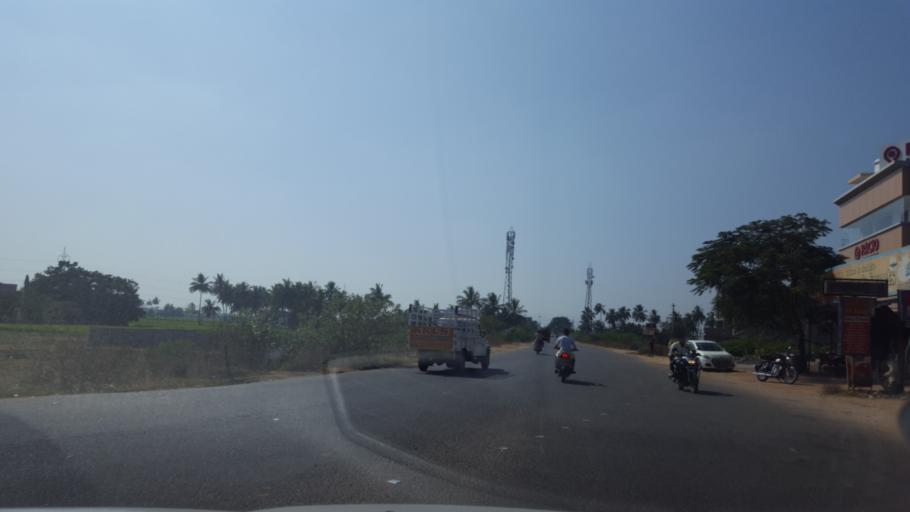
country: IN
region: Tamil Nadu
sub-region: Kancheepuram
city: Kanchipuram
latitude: 12.8678
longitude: 79.6535
